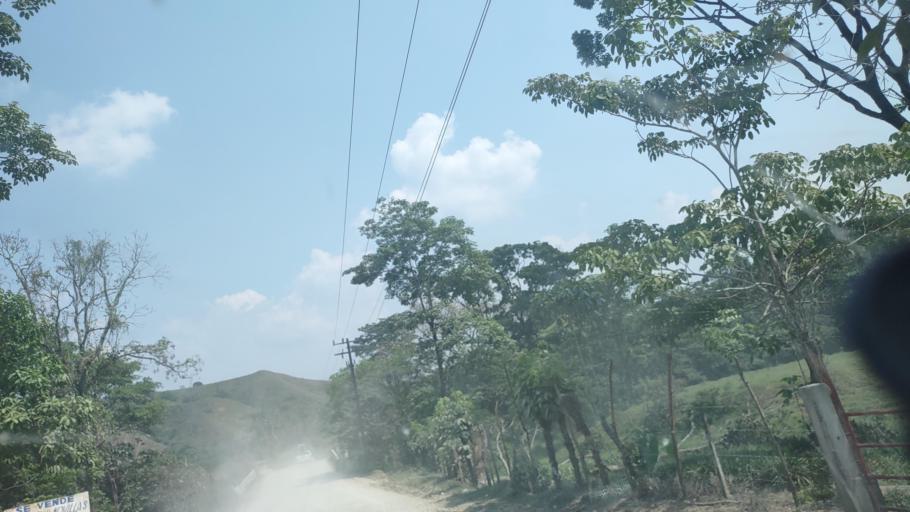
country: MX
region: Tabasco
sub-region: Huimanguillo
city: Francisco Rueda
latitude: 17.5810
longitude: -93.8903
